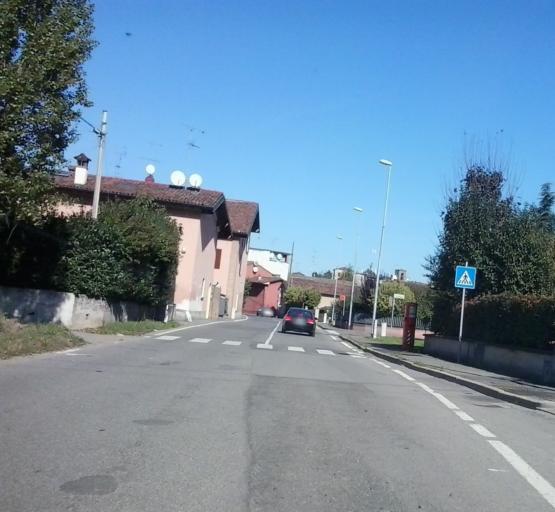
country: IT
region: Lombardy
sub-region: Provincia di Brescia
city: Poncarale
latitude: 45.4578
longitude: 10.1717
